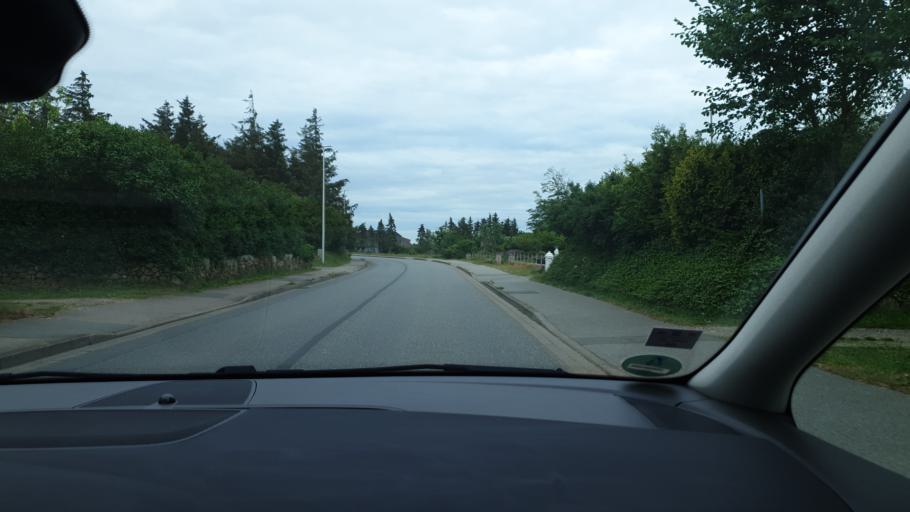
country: DE
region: Schleswig-Holstein
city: Schobull
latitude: 54.5146
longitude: 8.9961
